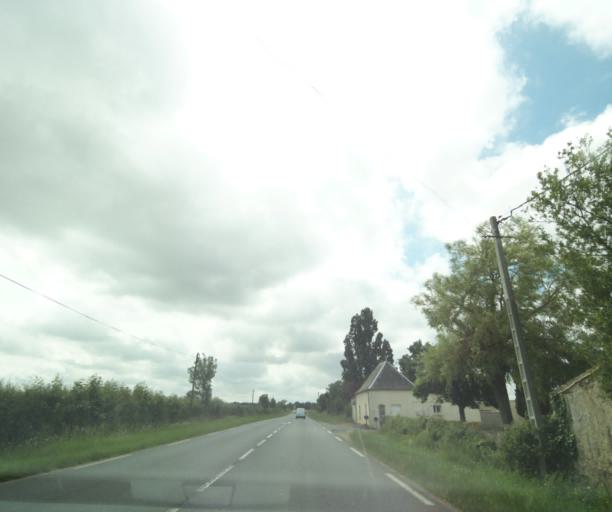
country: FR
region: Poitou-Charentes
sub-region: Departement des Deux-Sevres
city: Viennay
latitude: 46.7076
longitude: -0.2393
